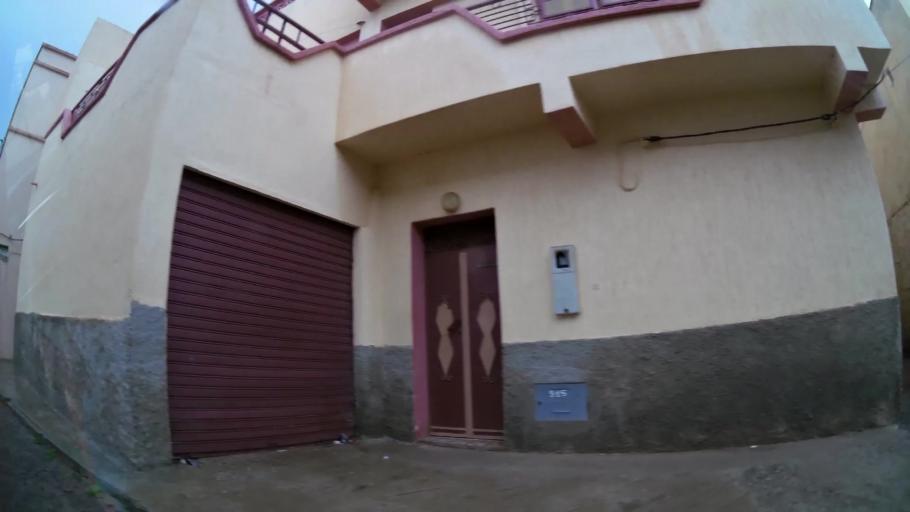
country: MA
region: Oriental
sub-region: Nador
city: Nador
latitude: 35.1556
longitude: -2.9553
